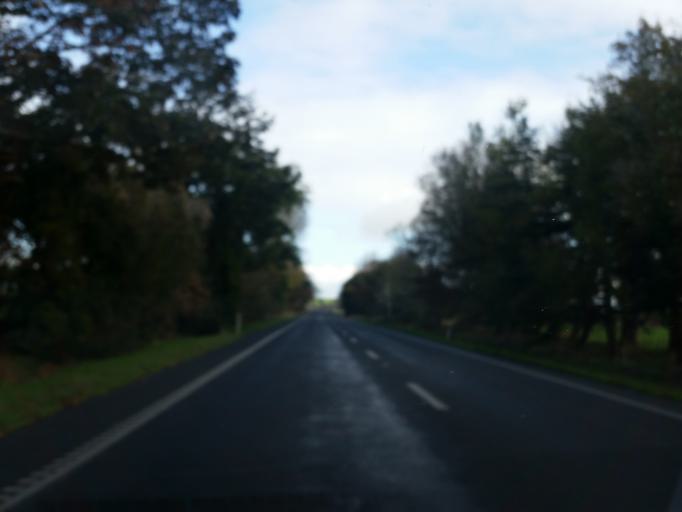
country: NZ
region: Waikato
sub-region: Hauraki District
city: Ngatea
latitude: -37.2802
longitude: 175.4274
